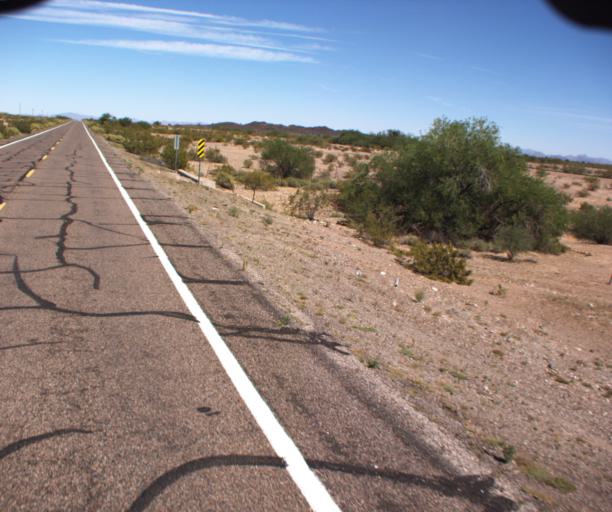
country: US
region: Arizona
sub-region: Maricopa County
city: Gila Bend
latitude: 32.7925
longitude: -112.8037
